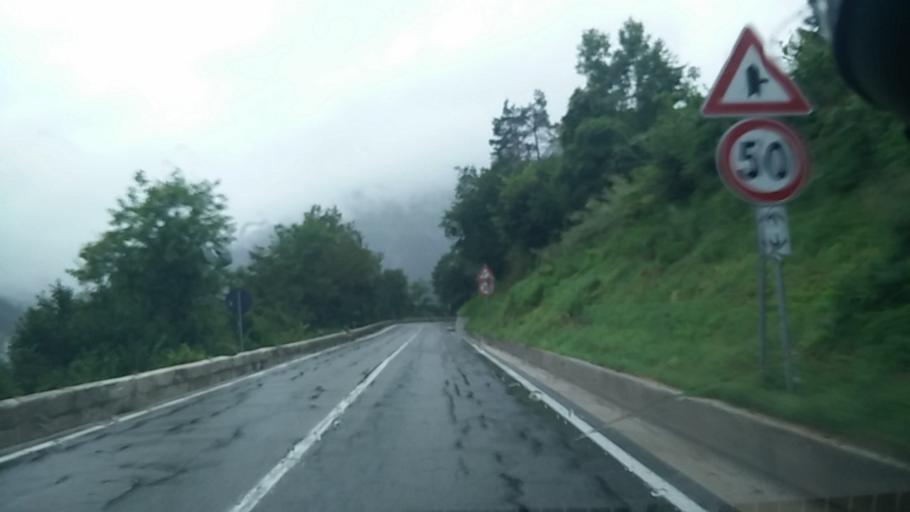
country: IT
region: Friuli Venezia Giulia
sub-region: Provincia di Udine
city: Tarvisio
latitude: 46.5067
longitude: 13.5954
